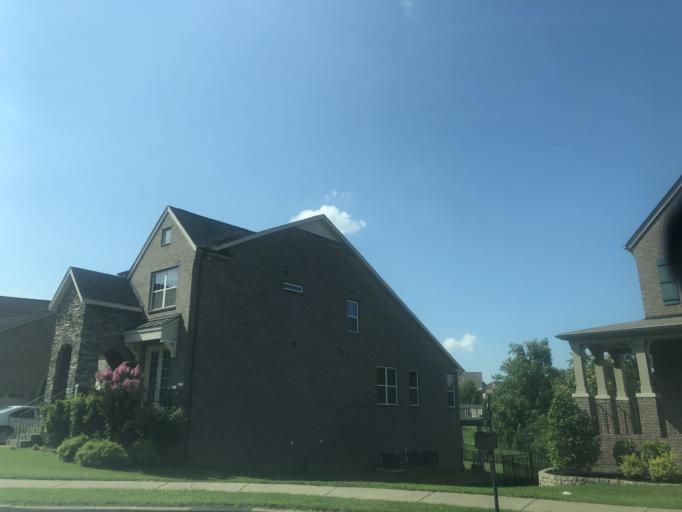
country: US
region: Tennessee
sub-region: Wilson County
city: Green Hill
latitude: 36.1412
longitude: -86.5901
